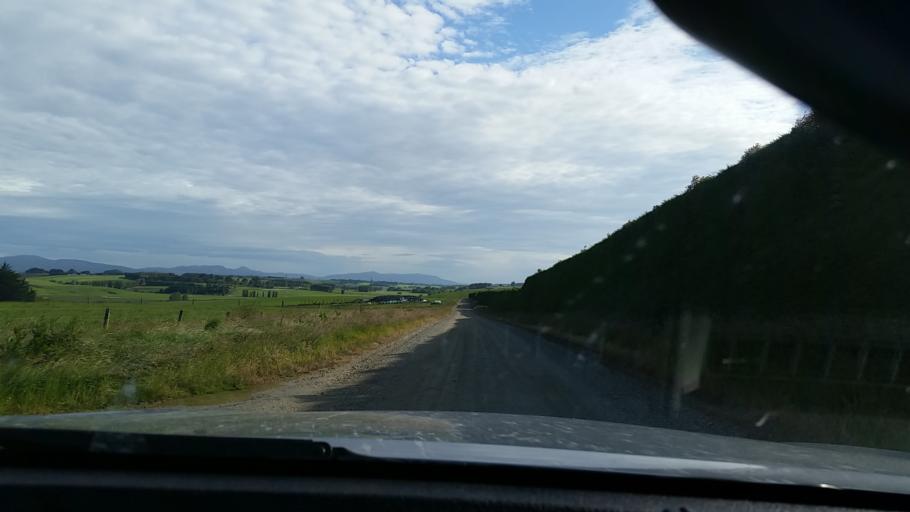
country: NZ
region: Southland
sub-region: Gore District
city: Gore
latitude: -46.2718
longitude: 168.7150
